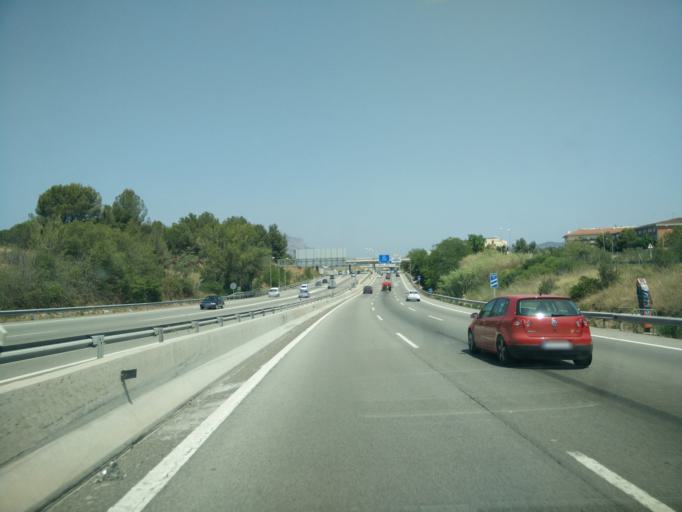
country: ES
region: Catalonia
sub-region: Provincia de Barcelona
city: Abrera
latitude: 41.5123
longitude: 1.9002
